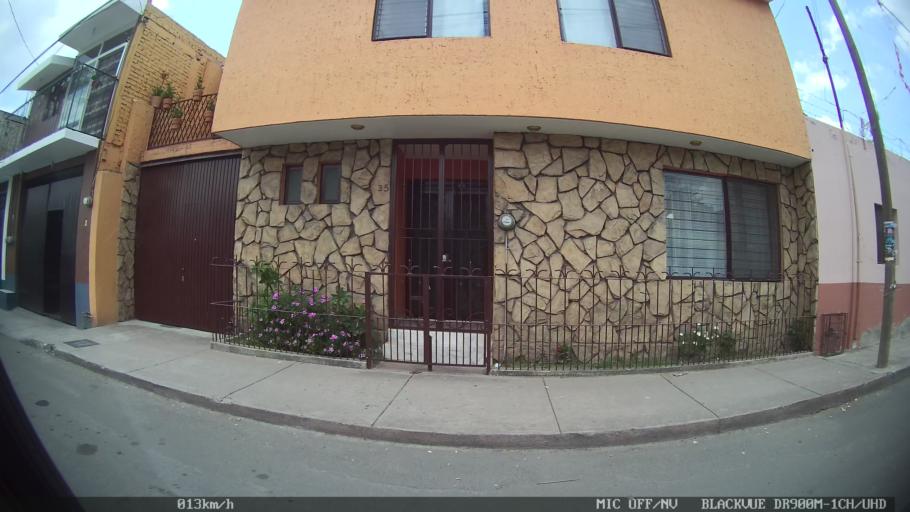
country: MX
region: Jalisco
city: Tonala
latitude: 20.6612
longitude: -103.2275
